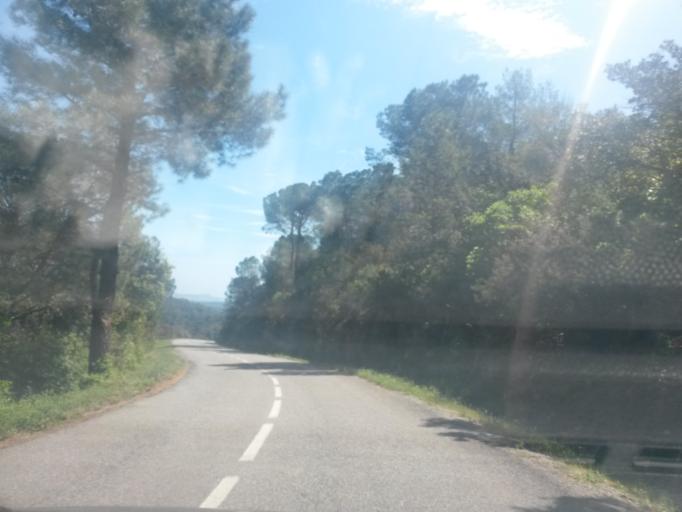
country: ES
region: Catalonia
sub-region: Provincia de Girona
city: Madremanya
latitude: 41.9818
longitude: 2.9345
